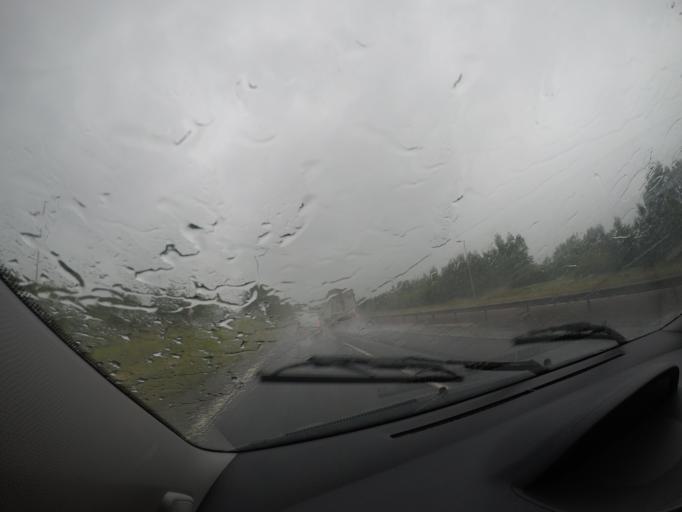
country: GB
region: Scotland
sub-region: Perth and Kinross
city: Errol
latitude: 56.4434
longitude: -3.1750
